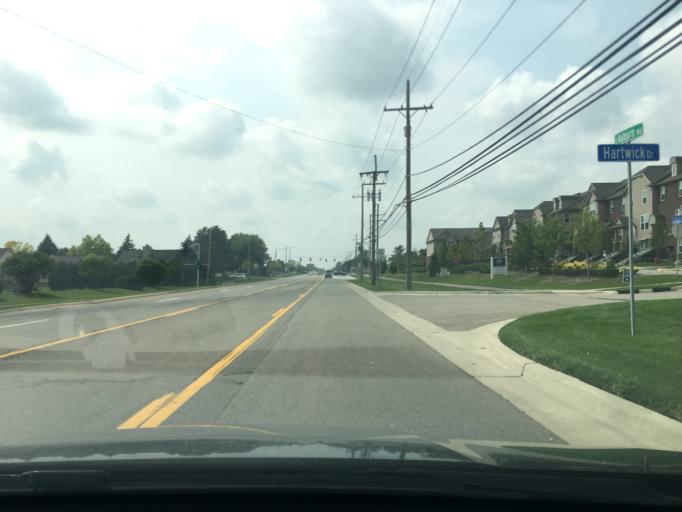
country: US
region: Michigan
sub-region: Oakland County
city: Rochester Hills
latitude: 42.6364
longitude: -83.1220
